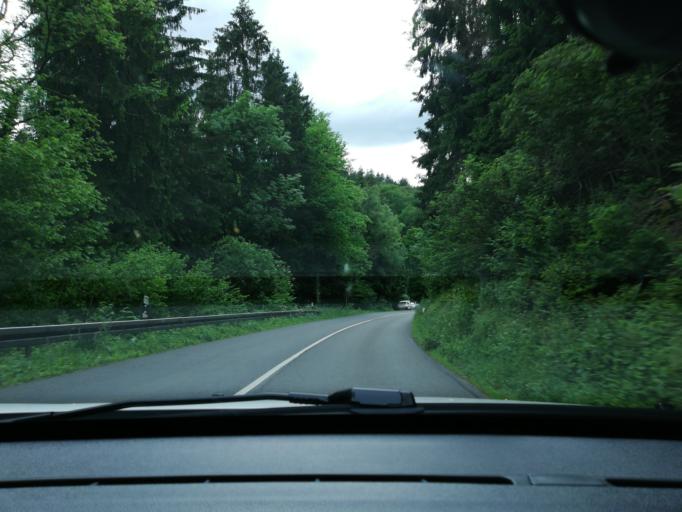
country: DE
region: North Rhine-Westphalia
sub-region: Regierungsbezirk Arnsberg
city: Schalksmuhle
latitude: 51.2343
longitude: 7.5584
